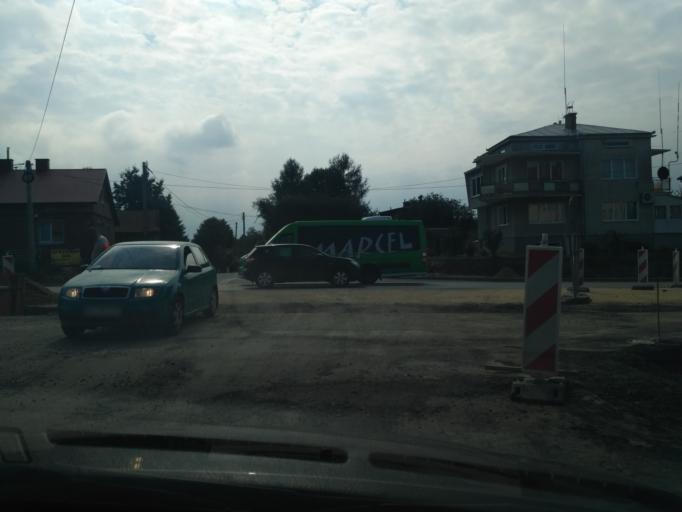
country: PL
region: Subcarpathian Voivodeship
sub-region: Powiat rzeszowski
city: Boguchwala
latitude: 50.0058
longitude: 21.9597
